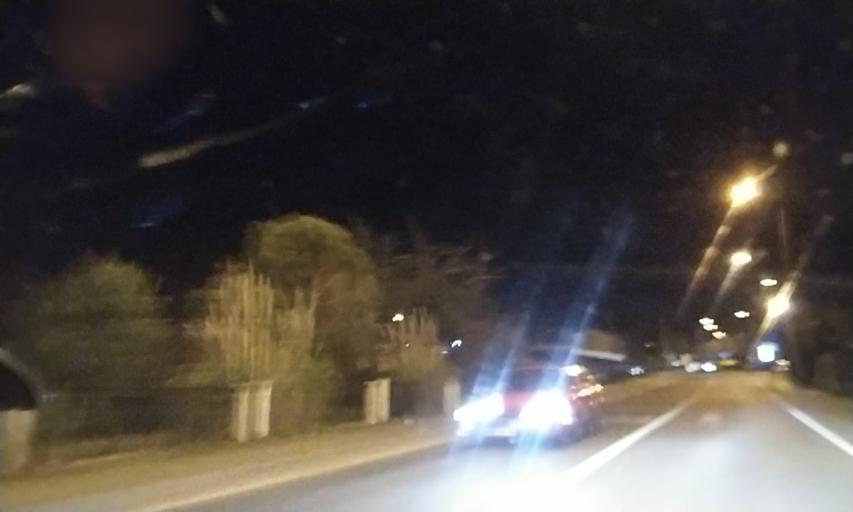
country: PT
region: Castelo Branco
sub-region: Concelho do Fundao
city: Fundao
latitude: 40.1641
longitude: -7.4972
